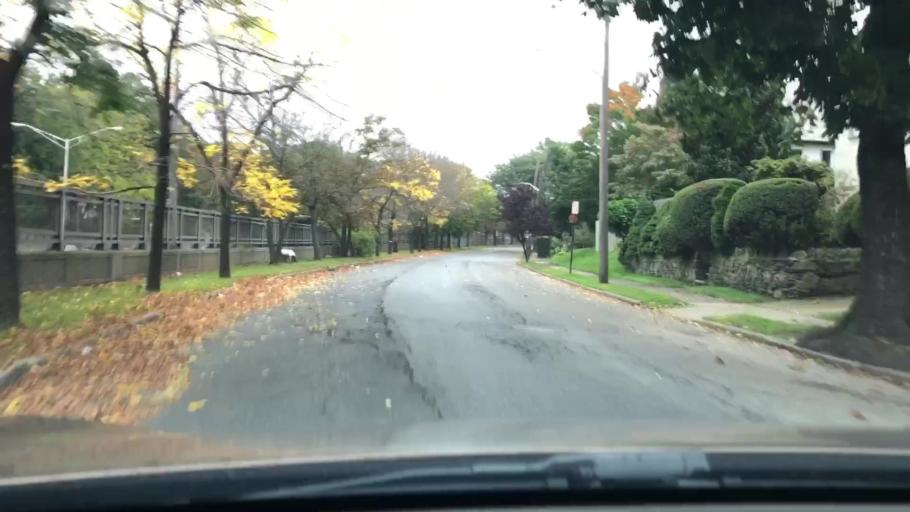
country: US
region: New York
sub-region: Westchester County
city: Bronxville
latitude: 40.9256
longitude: -73.8311
